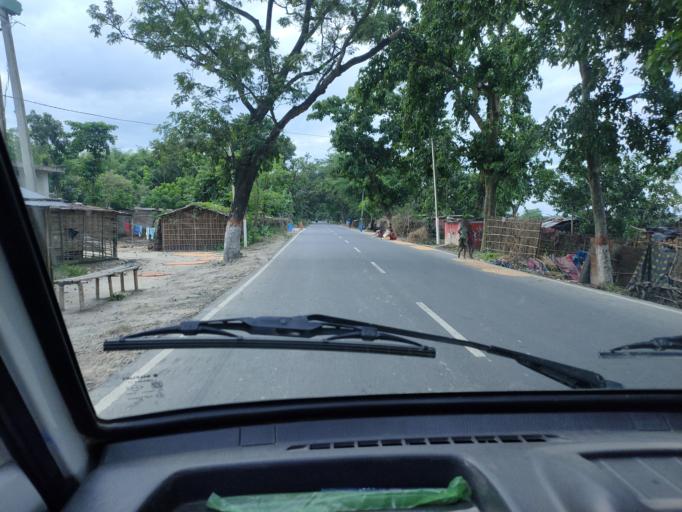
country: IN
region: West Bengal
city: Kishanganj
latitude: 26.1708
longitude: 87.9122
